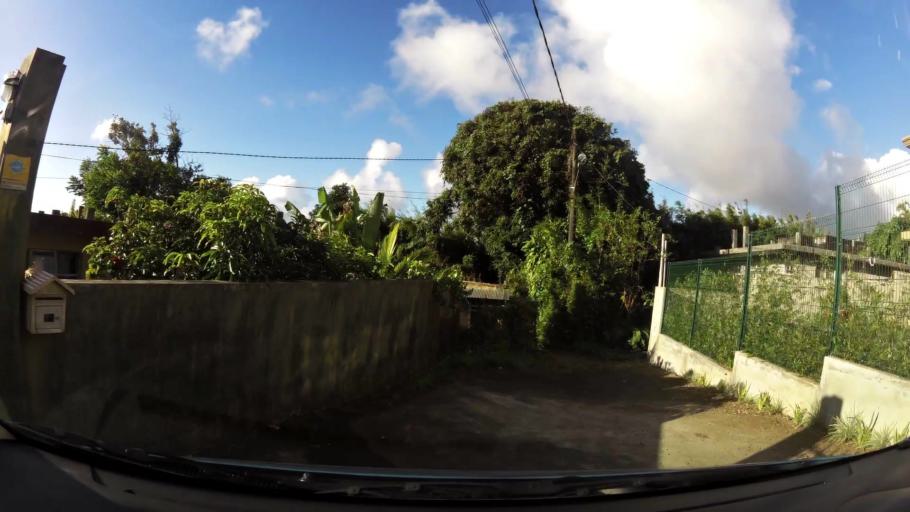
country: MU
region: Plaines Wilhems
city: Curepipe
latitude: -20.3158
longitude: 57.5133
